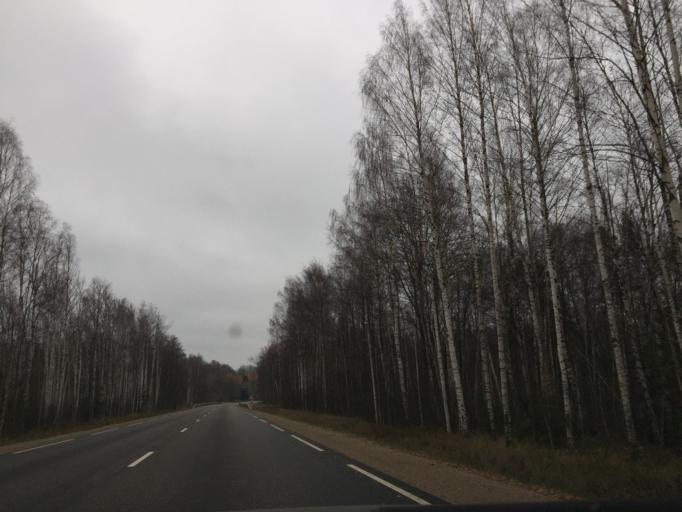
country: LV
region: Pargaujas
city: Stalbe
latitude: 57.5127
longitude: 25.0009
